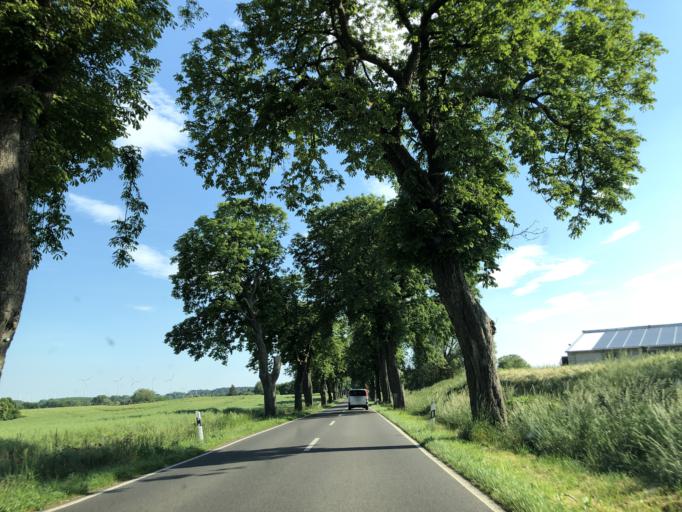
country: DE
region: Brandenburg
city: Angermunde
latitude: 53.1009
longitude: 13.9643
